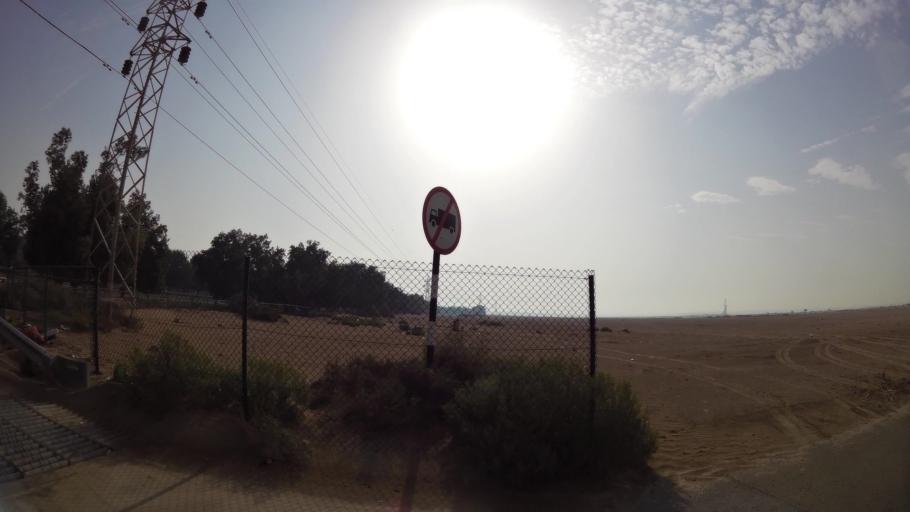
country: AE
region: Abu Dhabi
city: Abu Dhabi
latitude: 24.2644
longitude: 54.6755
